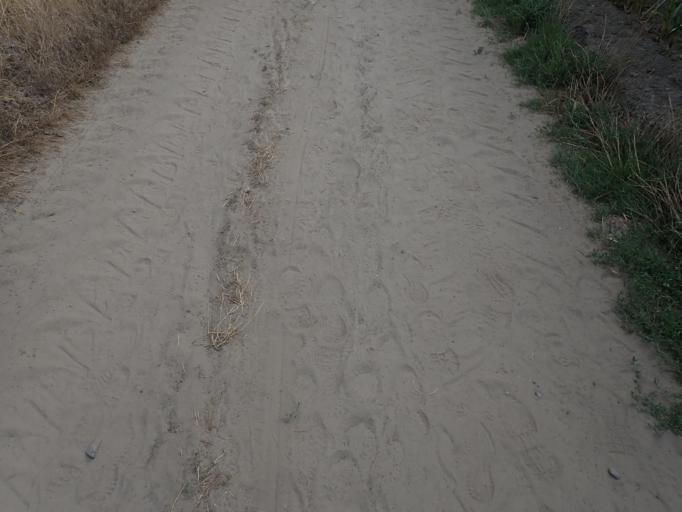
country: BE
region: Flanders
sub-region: Provincie Vlaams-Brabant
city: Kapelle-op-den-Bos
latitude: 51.0359
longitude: 4.3863
